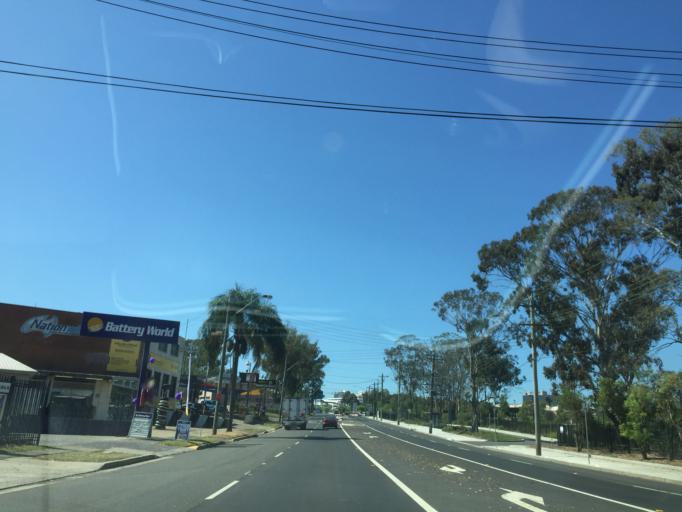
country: AU
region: New South Wales
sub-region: Blacktown
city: Blacktown
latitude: -33.7645
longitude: 150.9027
